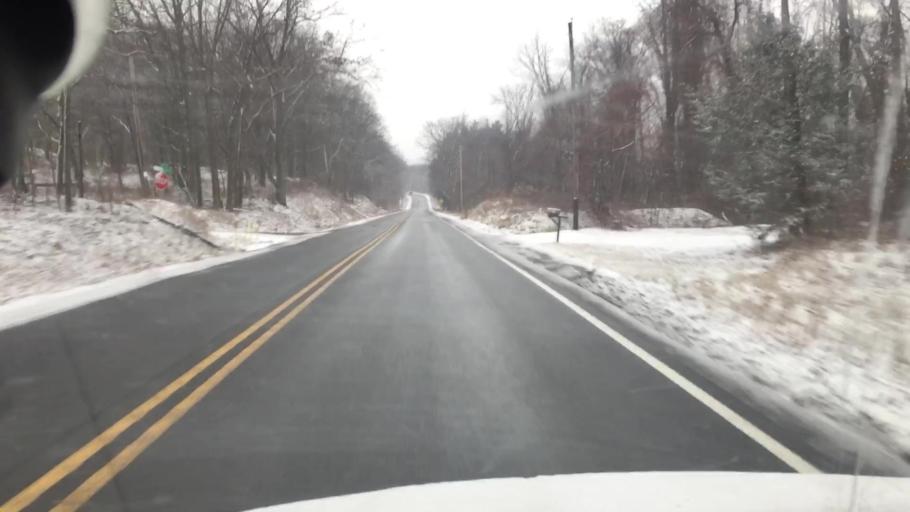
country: US
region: Pennsylvania
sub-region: Luzerne County
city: Conyngham
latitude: 41.0320
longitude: -76.1043
